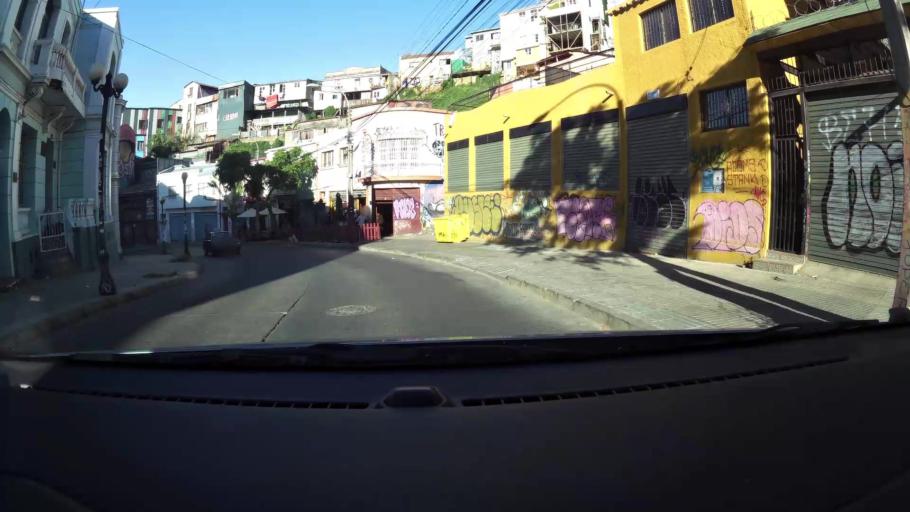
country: CL
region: Valparaiso
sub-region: Provincia de Valparaiso
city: Valparaiso
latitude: -33.0472
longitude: -71.6250
